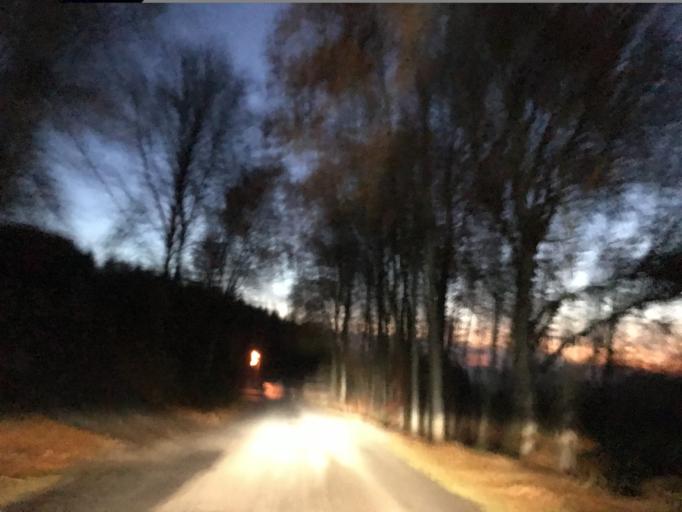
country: FR
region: Rhone-Alpes
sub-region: Departement de la Loire
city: Noiretable
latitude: 45.7228
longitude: 3.7339
